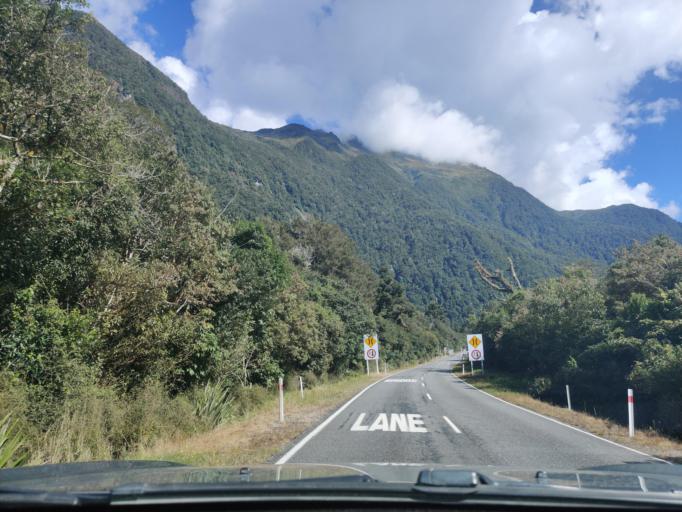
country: NZ
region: Otago
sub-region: Queenstown-Lakes District
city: Wanaka
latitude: -43.9678
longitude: 169.1697
